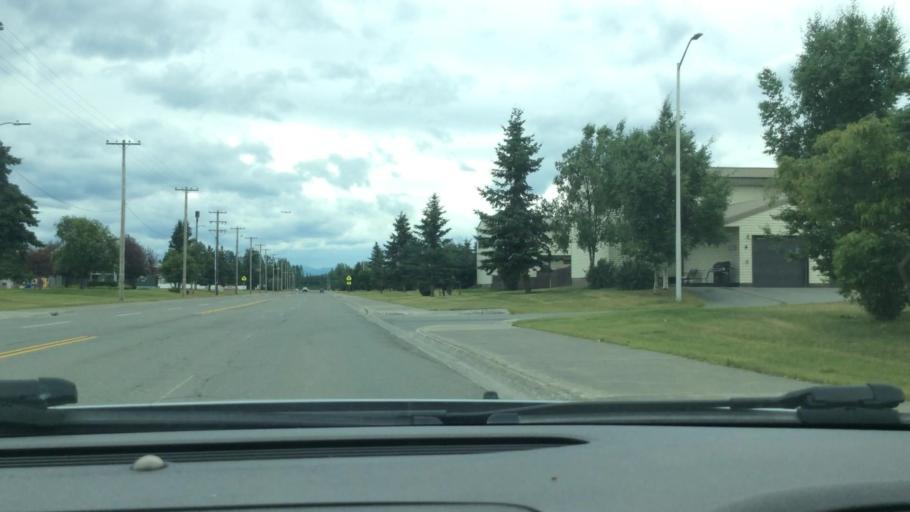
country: US
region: Alaska
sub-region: Anchorage Municipality
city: Anchorage
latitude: 61.2347
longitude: -149.8493
